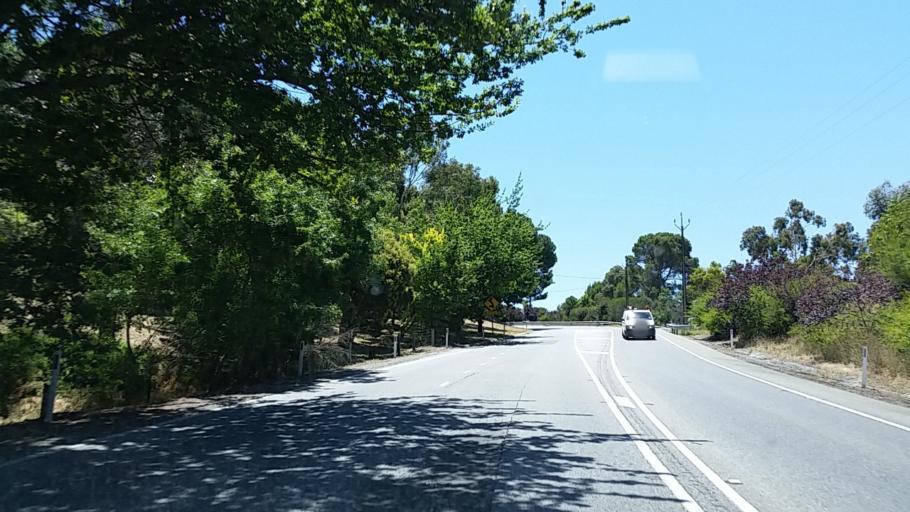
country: AU
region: South Australia
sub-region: Tea Tree Gully
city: Golden Grove
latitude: -34.8235
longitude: 138.7566
